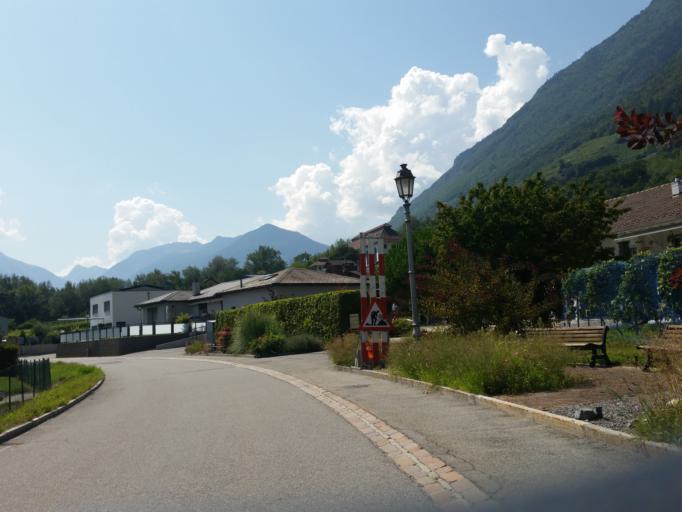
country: CH
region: Valais
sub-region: Martigny District
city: Fully
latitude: 46.1442
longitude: 7.1216
